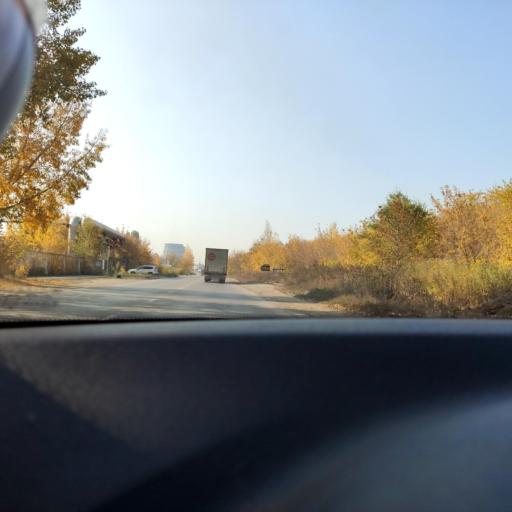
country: RU
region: Samara
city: Petra-Dubrava
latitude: 53.2573
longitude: 50.2841
